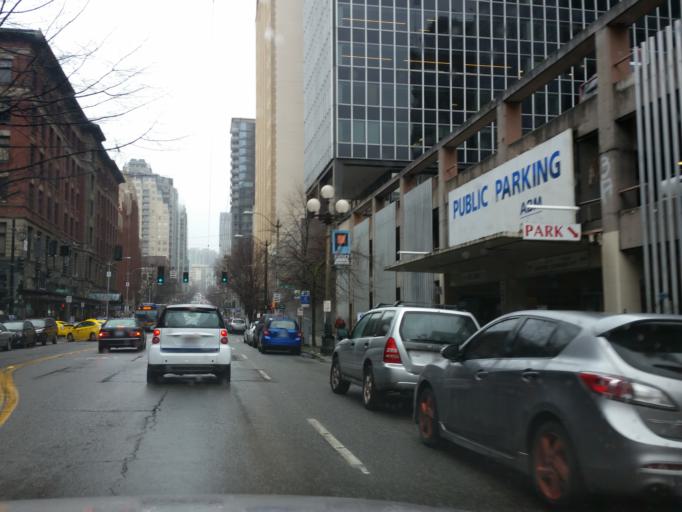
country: US
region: Washington
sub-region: King County
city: Seattle
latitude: 47.6028
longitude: -122.3344
